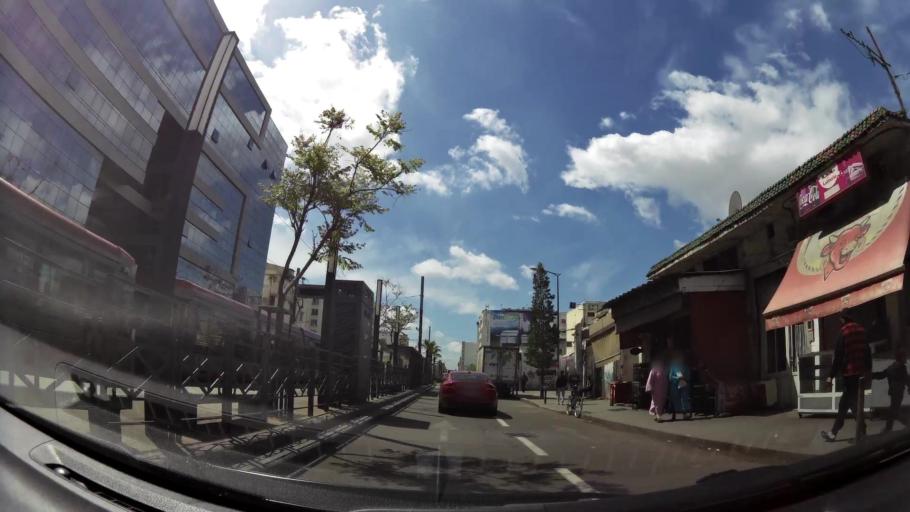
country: MA
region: Grand Casablanca
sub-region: Casablanca
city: Casablanca
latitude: 33.5749
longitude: -7.6258
